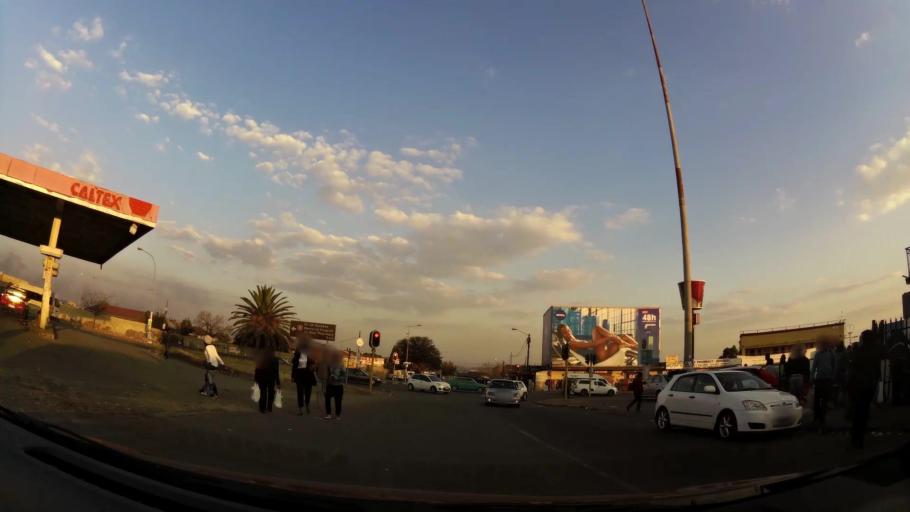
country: ZA
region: Gauteng
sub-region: City of Johannesburg Metropolitan Municipality
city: Soweto
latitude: -26.2368
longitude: 27.9015
